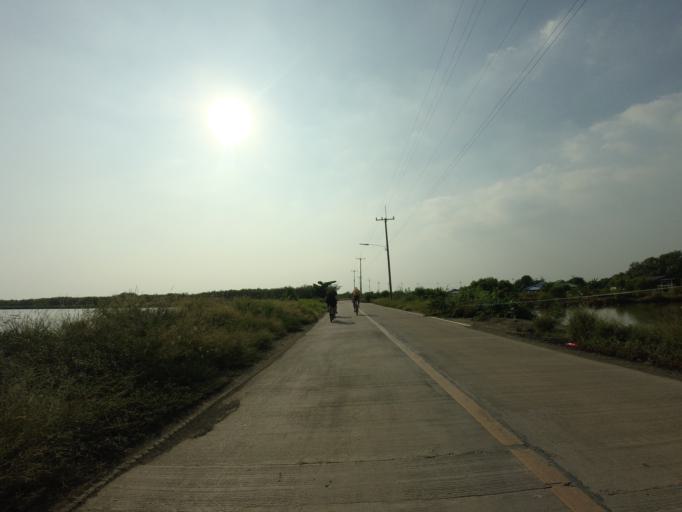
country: TH
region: Samut Sakhon
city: Samut Sakhon
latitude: 13.4980
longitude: 100.3329
